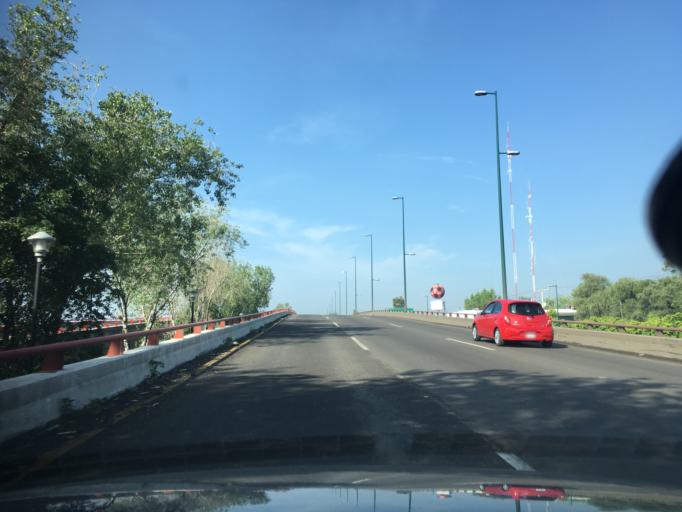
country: MX
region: Michoacan
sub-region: Tarimbaro
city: Fraccionamiento Metropolis II
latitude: 19.7208
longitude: -101.2272
